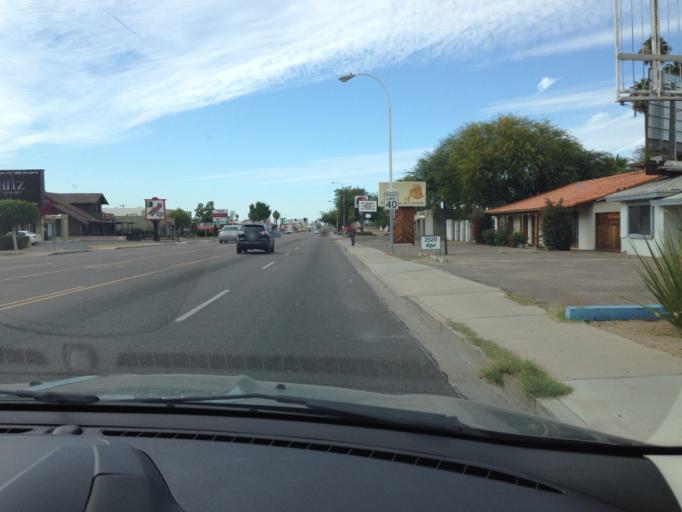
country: US
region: Arizona
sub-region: Maricopa County
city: Phoenix
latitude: 33.4950
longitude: -112.0270
